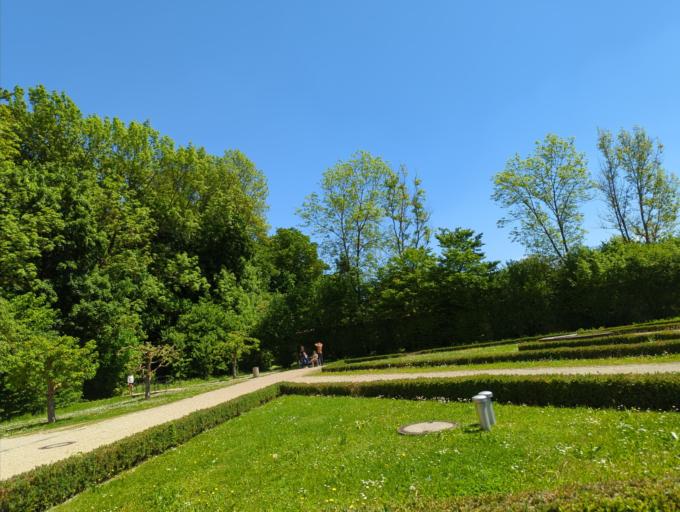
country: DE
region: Bavaria
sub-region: Upper Palatinate
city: Alteglofsheim
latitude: 48.9180
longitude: 12.2050
